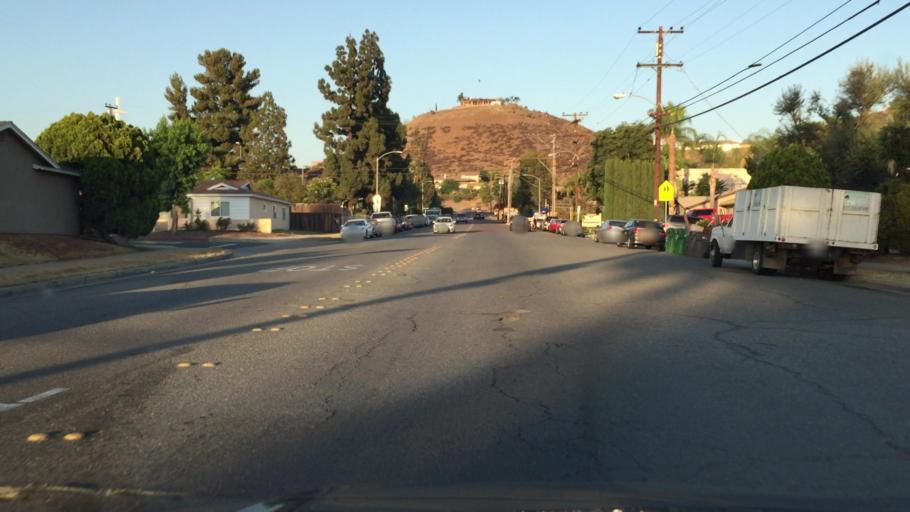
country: US
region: California
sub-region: San Diego County
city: Bostonia
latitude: 32.8191
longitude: -116.9484
